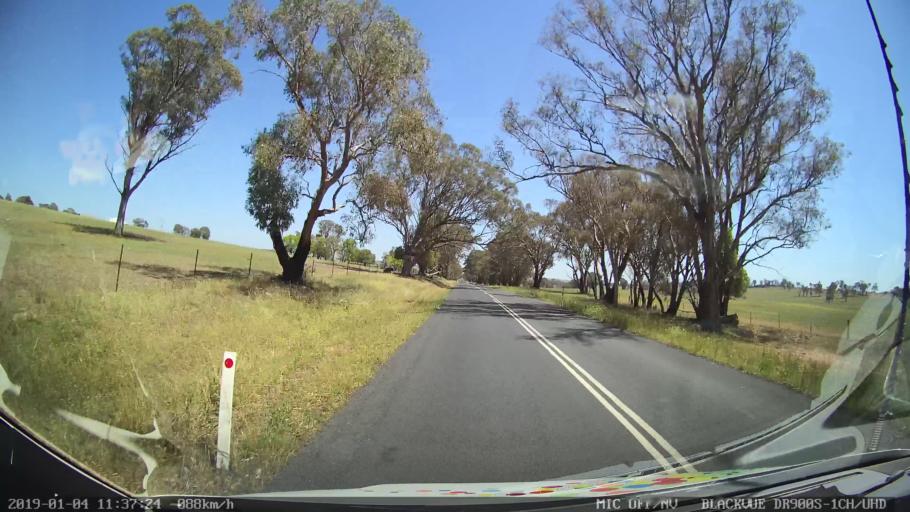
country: AU
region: New South Wales
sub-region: Cabonne
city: Molong
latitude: -33.0328
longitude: 148.8077
